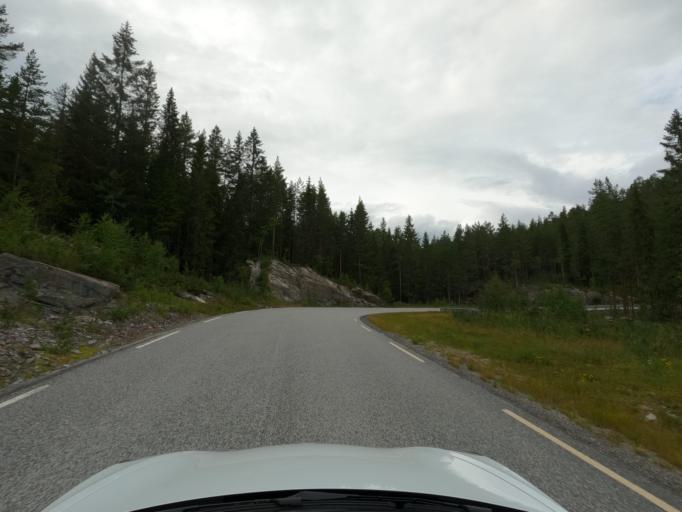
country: NO
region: Telemark
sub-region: Notodden
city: Notodden
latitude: 59.7006
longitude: 9.1318
